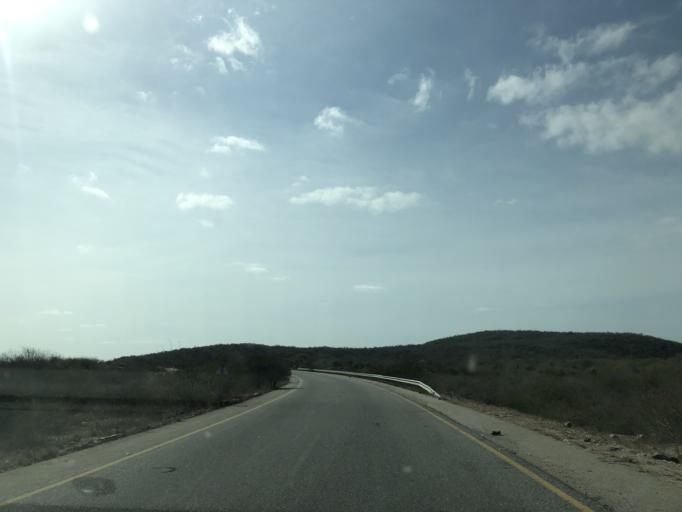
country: AO
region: Benguela
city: Benguela
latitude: -12.8941
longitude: 13.4933
